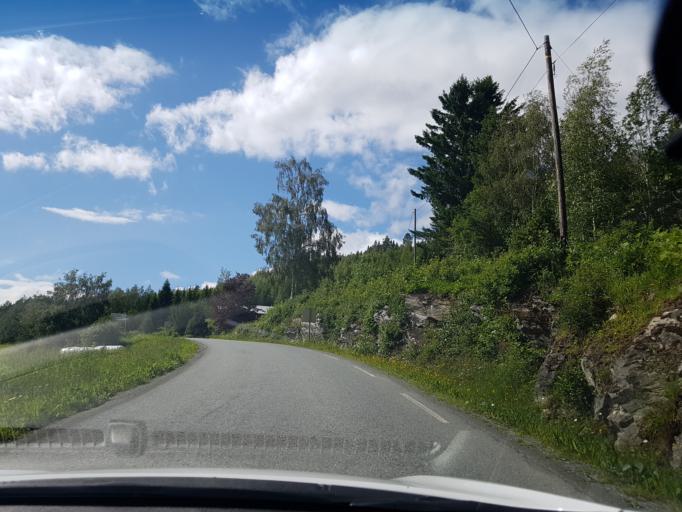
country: NO
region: Nord-Trondelag
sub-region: Frosta
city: Frosta
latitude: 63.6061
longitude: 10.8444
